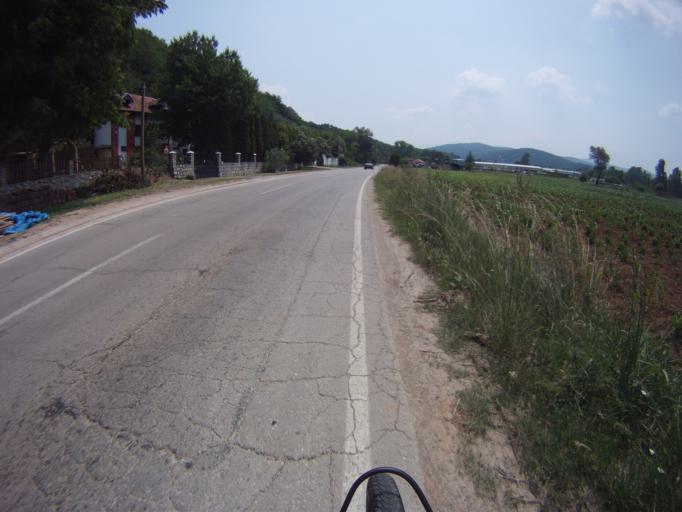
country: RS
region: Central Serbia
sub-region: Nisavski Okrug
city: Gadzin Han
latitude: 43.2319
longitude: 22.0298
